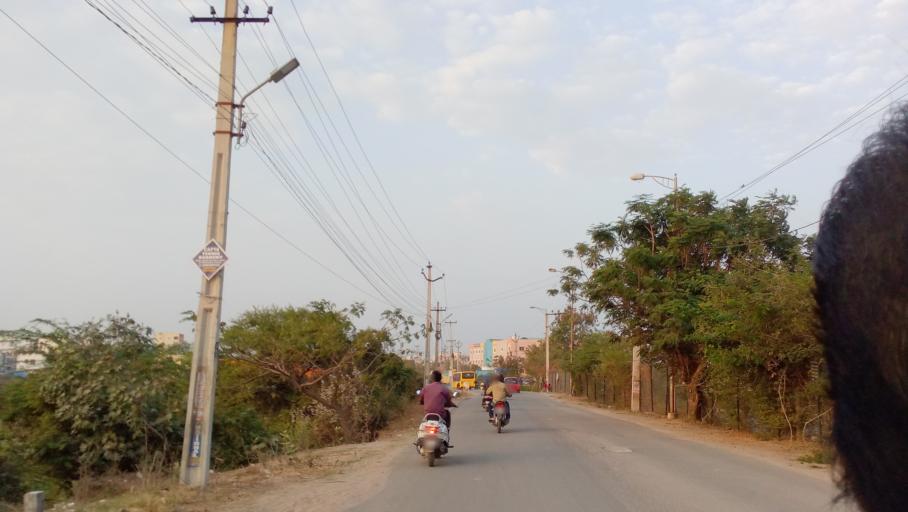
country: IN
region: Telangana
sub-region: Medak
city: Serilingampalle
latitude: 17.5137
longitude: 78.3187
